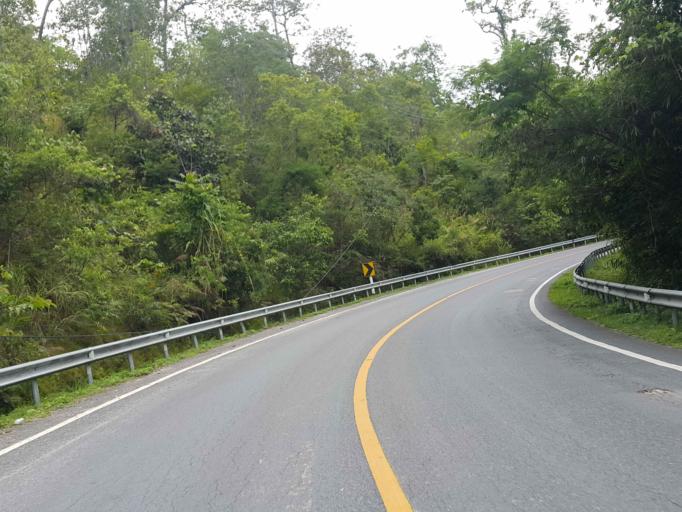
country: TH
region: Chiang Mai
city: Chom Thong
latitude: 18.5286
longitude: 98.6261
